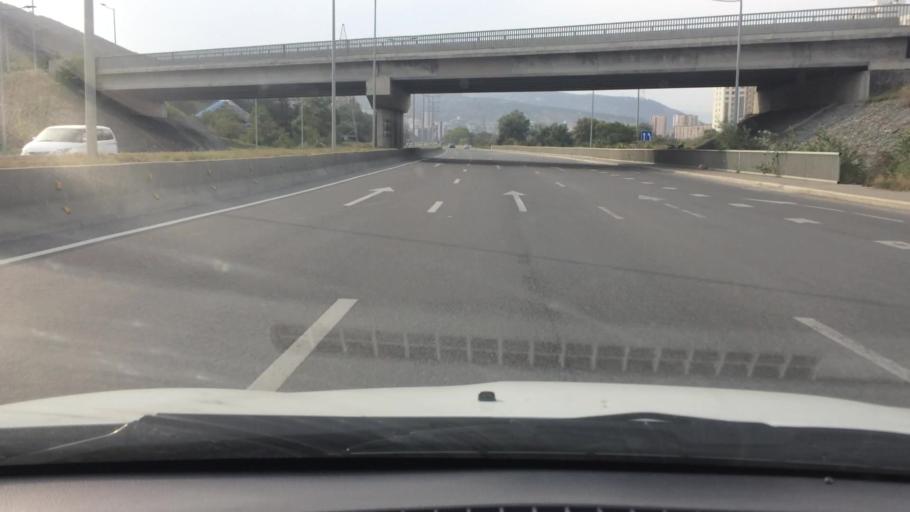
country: GE
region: T'bilisi
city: Tbilisi
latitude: 41.6693
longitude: 44.8590
